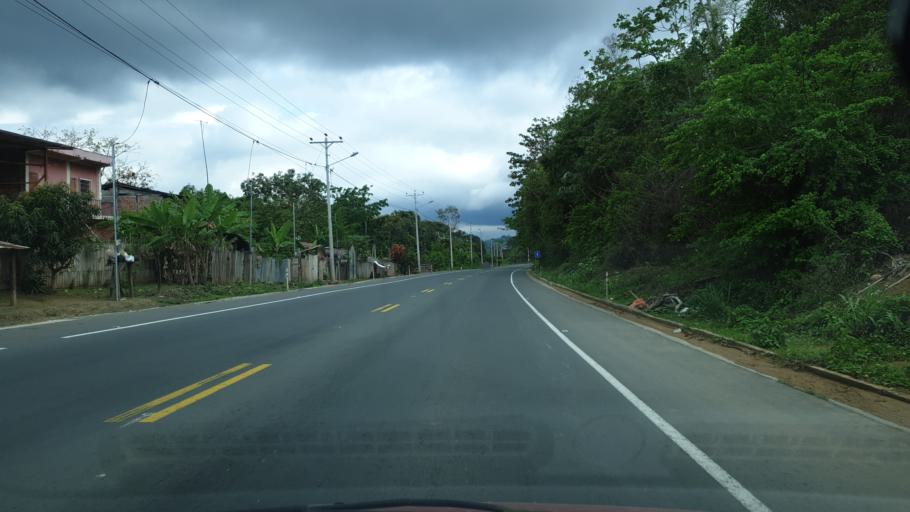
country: EC
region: Manabi
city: Pajan
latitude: -1.5596
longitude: -80.5253
